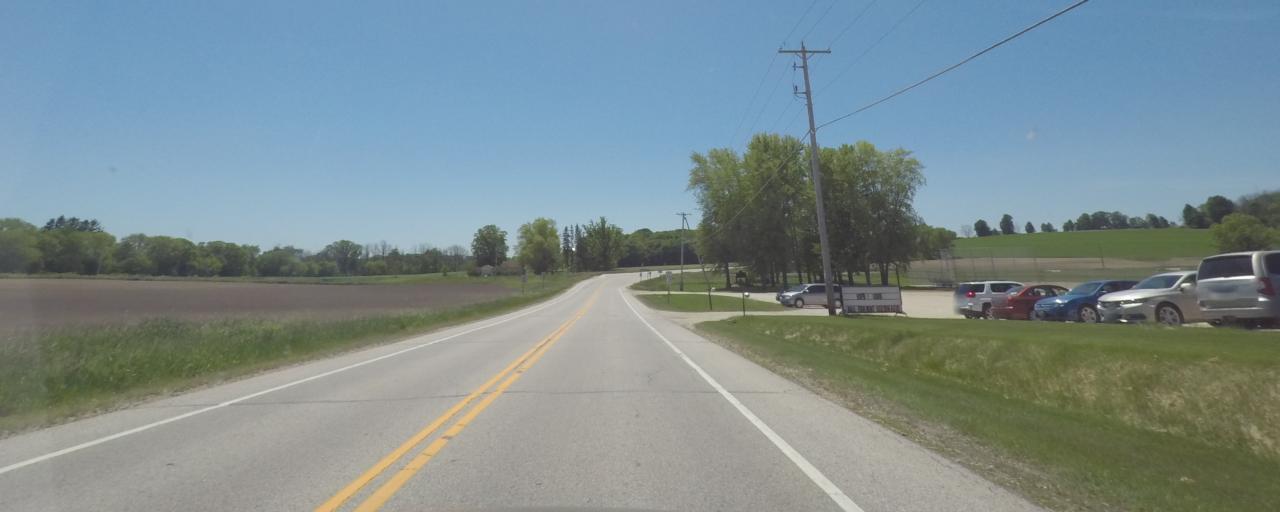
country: US
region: Wisconsin
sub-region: Ozaukee County
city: Kohler
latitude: 43.5881
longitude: -88.0505
